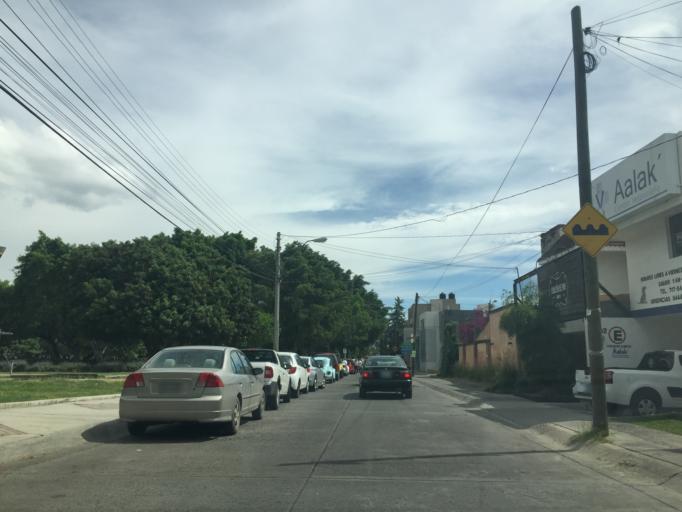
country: MX
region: Guanajuato
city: Leon
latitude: 21.1527
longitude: -101.6944
